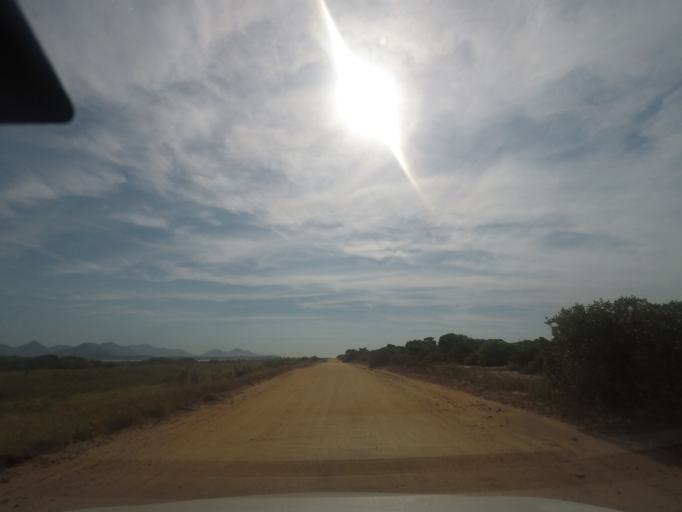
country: BR
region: Rio de Janeiro
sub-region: Marica
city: Marica
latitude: -22.9596
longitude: -42.8730
